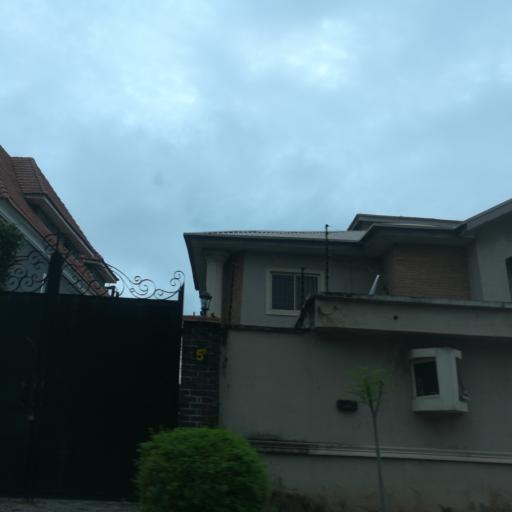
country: NG
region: Lagos
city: Ikoyi
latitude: 6.4417
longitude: 3.4695
